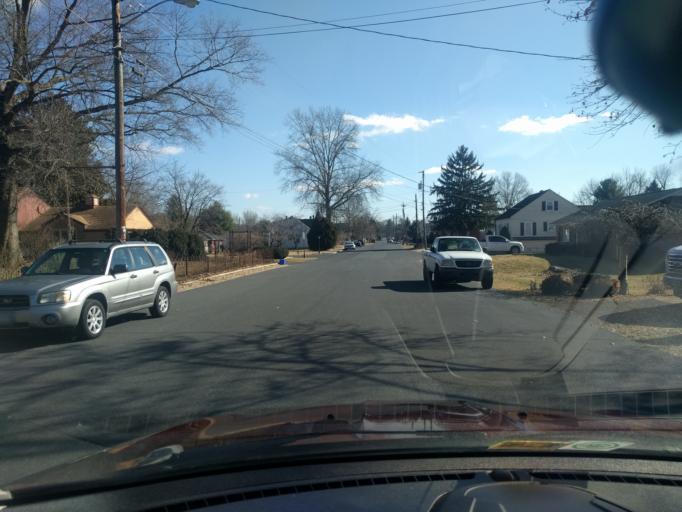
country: US
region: Virginia
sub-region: Rockingham County
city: Bridgewater
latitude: 38.3851
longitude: -78.9783
